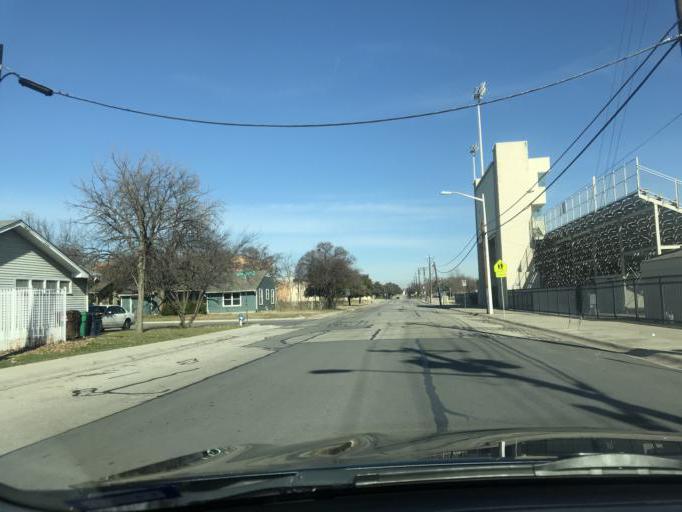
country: US
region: Texas
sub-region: Denton County
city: Denton
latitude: 33.2220
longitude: -97.1434
